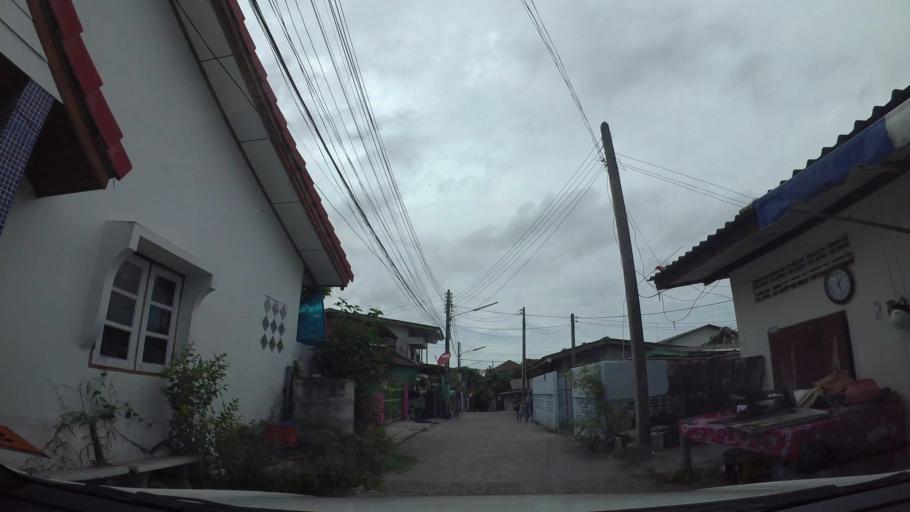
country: TH
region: Rayong
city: Rayong
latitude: 12.6642
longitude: 101.2694
